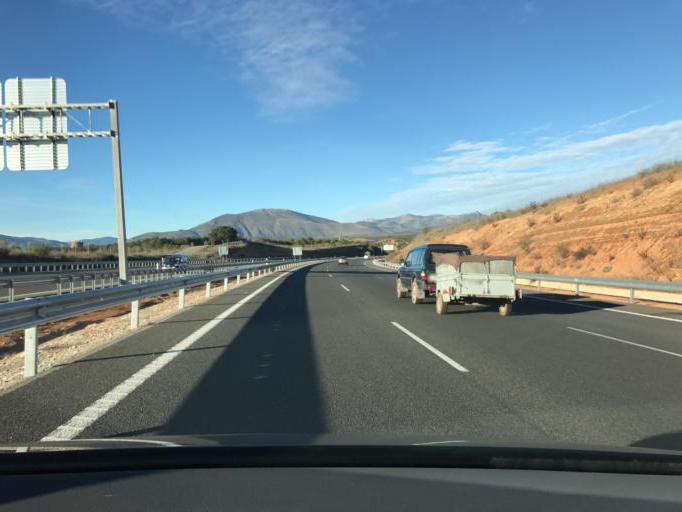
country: ES
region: Andalusia
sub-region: Provincia de Granada
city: Albolote
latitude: 37.2756
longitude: -3.6586
